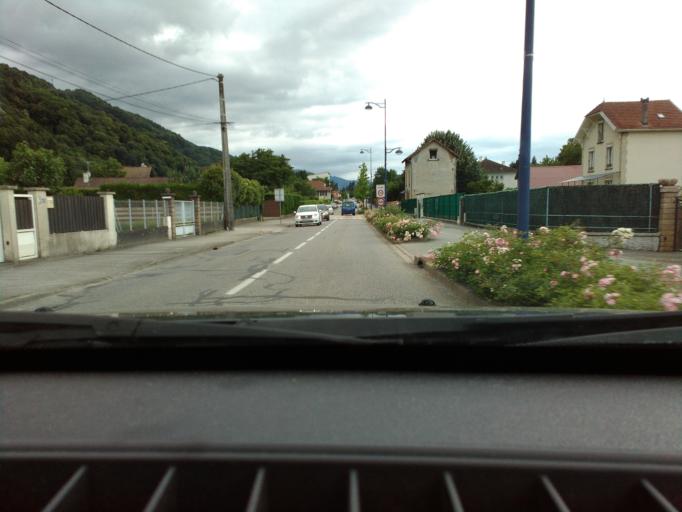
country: FR
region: Rhone-Alpes
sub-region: Departement de l'Isere
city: Villard-Bonnot
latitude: 45.2551
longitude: 5.9048
